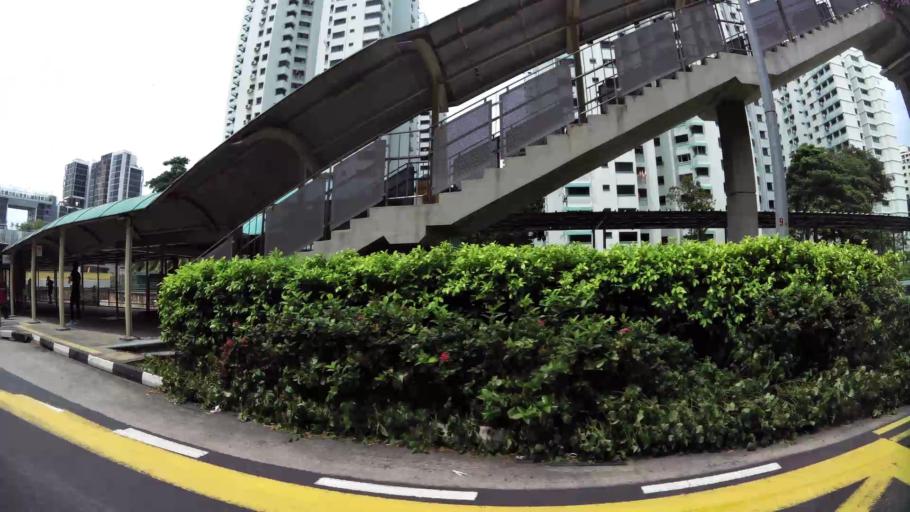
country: MY
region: Johor
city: Johor Bahru
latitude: 1.3805
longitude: 103.7624
